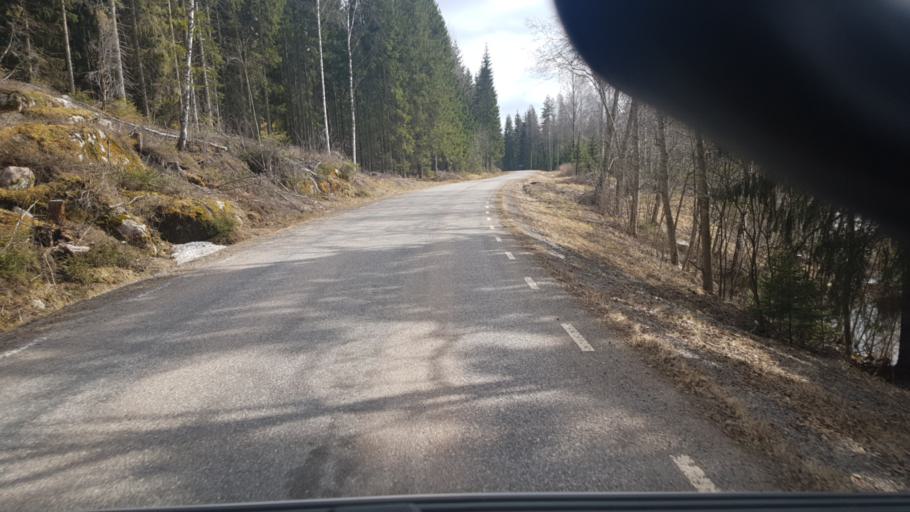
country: SE
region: Vaermland
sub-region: Eda Kommun
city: Amotfors
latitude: 59.8308
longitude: 12.4367
